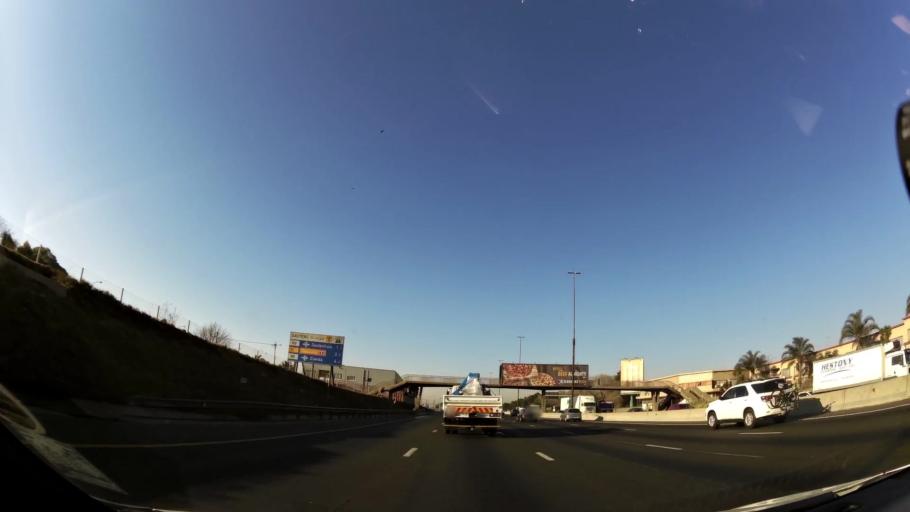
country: ZA
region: Gauteng
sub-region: Ekurhuleni Metropolitan Municipality
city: Germiston
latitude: -26.1982
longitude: 28.1328
